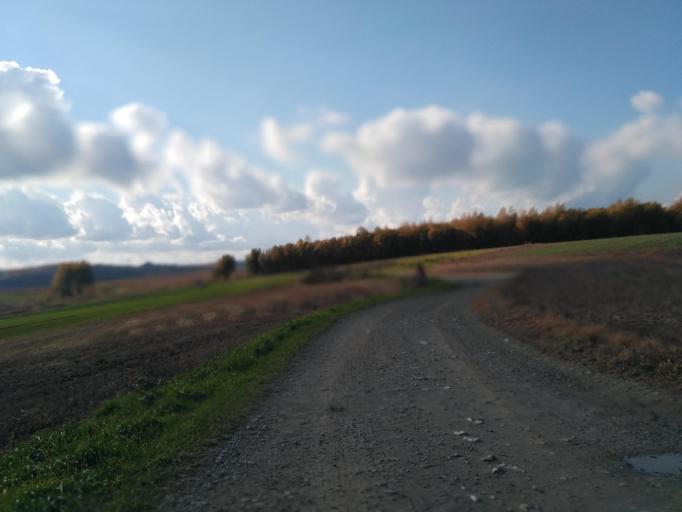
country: PL
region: Subcarpathian Voivodeship
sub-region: Powiat rzeszowski
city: Zglobien
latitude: 50.0007
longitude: 21.8602
